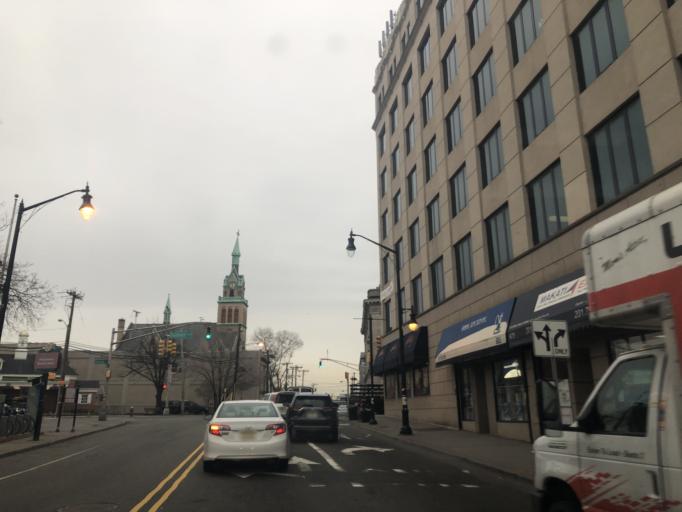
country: US
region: New Jersey
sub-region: Hudson County
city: Jersey City
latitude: 40.7350
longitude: -74.0599
